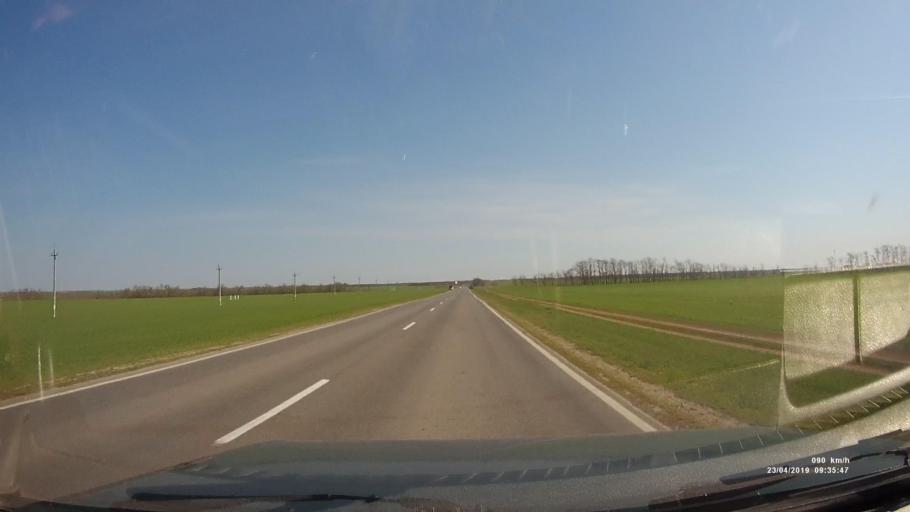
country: RU
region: Rostov
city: Gundorovskiy
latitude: 46.8261
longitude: 41.8739
